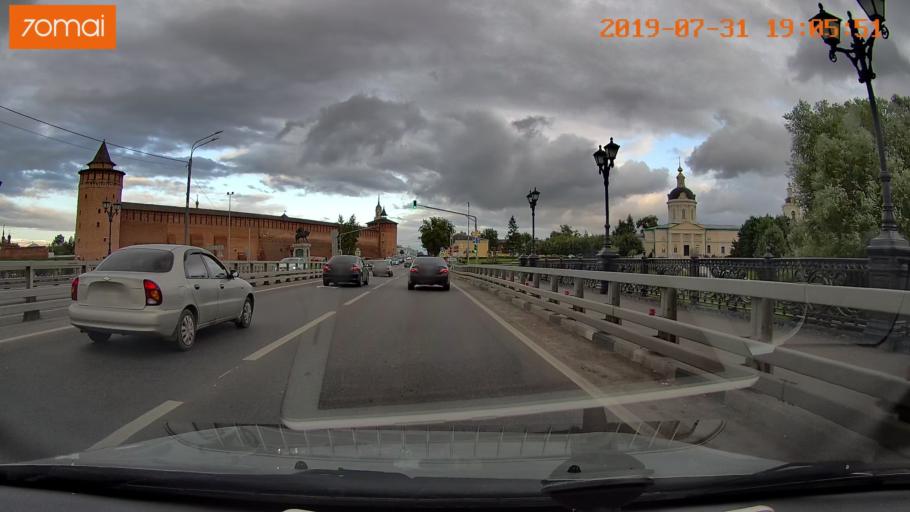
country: RU
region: Moskovskaya
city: Raduzhnyy
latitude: 55.1046
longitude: 38.7488
